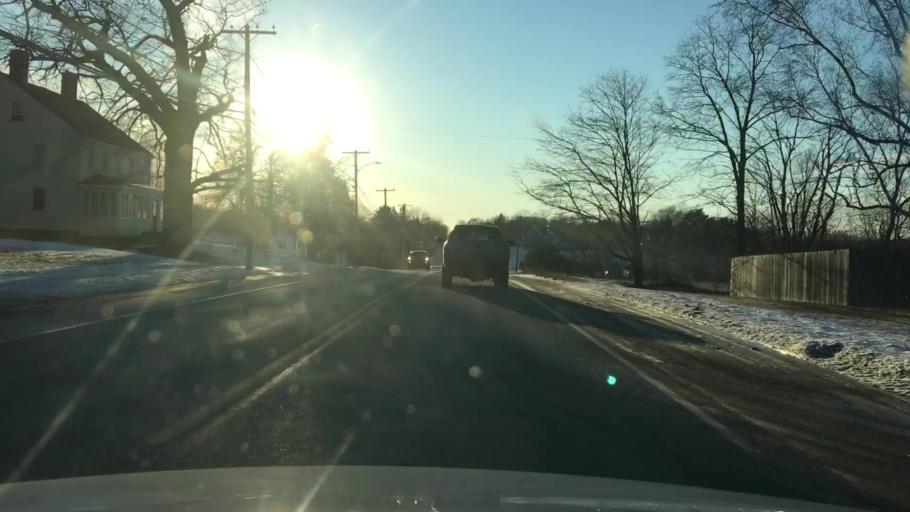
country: US
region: Maine
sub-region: Penobscot County
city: Brewer
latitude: 44.8033
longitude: -68.7470
